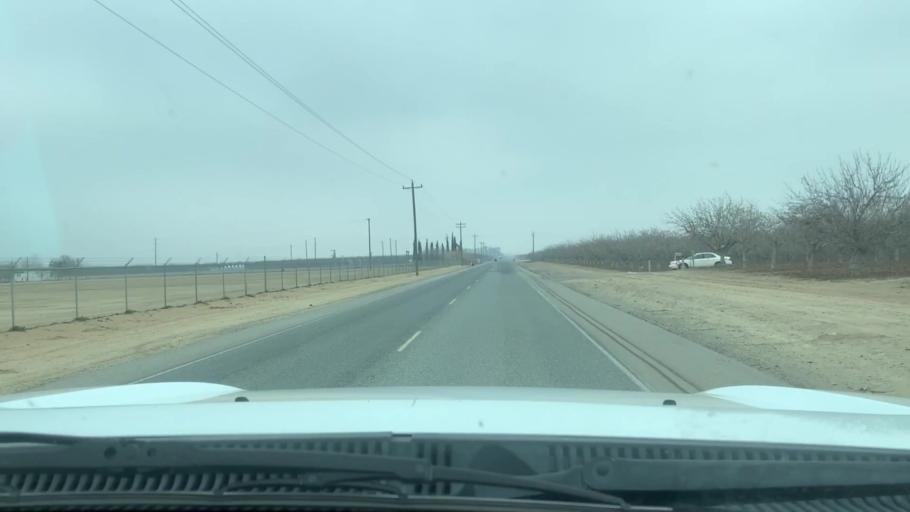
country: US
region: California
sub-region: Kern County
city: Buttonwillow
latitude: 35.5006
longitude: -119.4976
